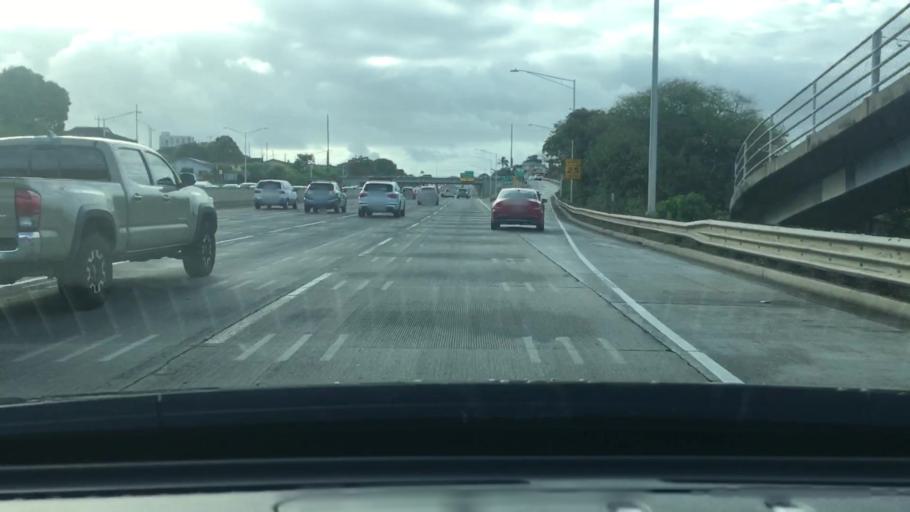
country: US
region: Hawaii
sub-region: Honolulu County
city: Honolulu
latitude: 21.2850
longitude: -157.8097
